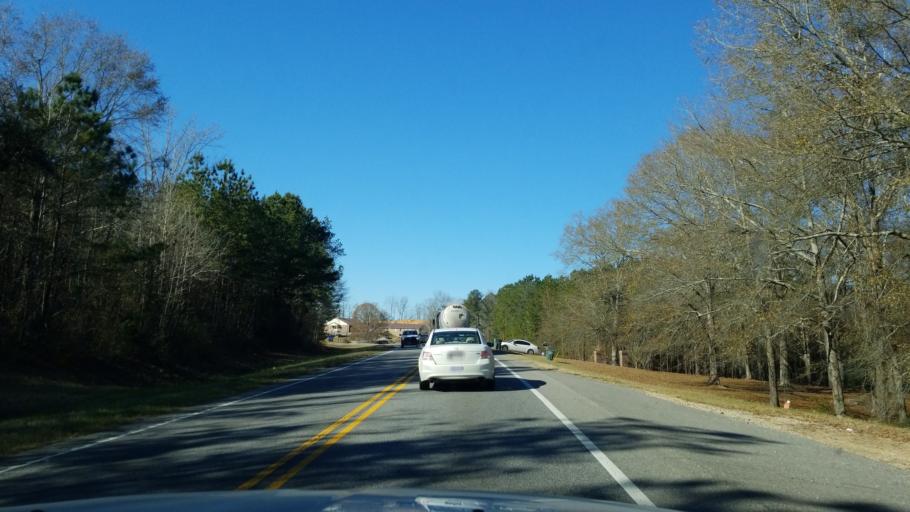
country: US
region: Alabama
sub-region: Pickens County
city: Gordo
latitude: 33.3304
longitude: -87.9131
